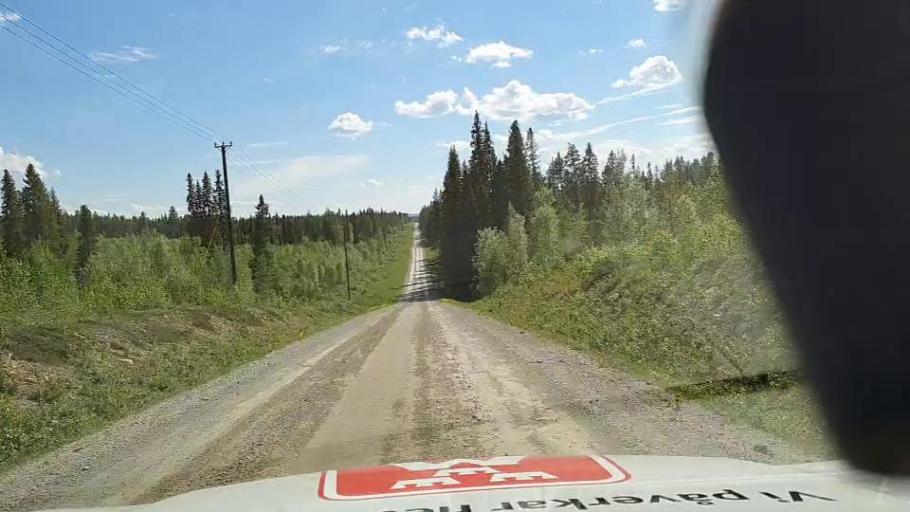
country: SE
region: Jaemtland
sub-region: Stroemsunds Kommun
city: Stroemsund
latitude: 64.4858
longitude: 15.5916
